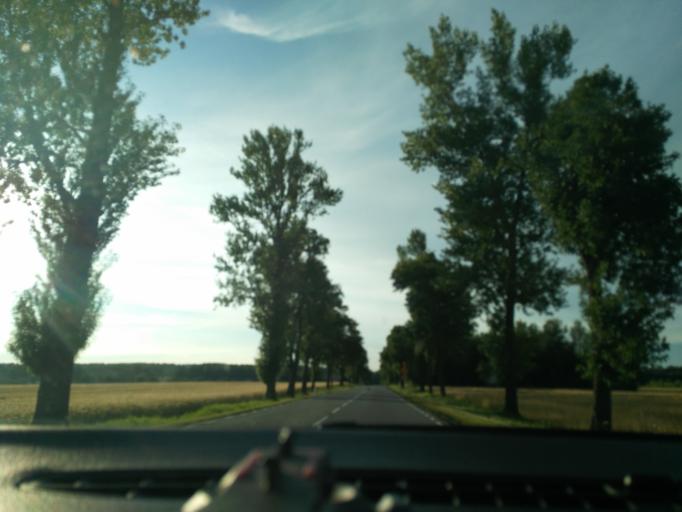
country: PL
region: Lublin Voivodeship
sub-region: Powiat krasnicki
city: Szastarka
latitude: 50.8398
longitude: 22.2994
